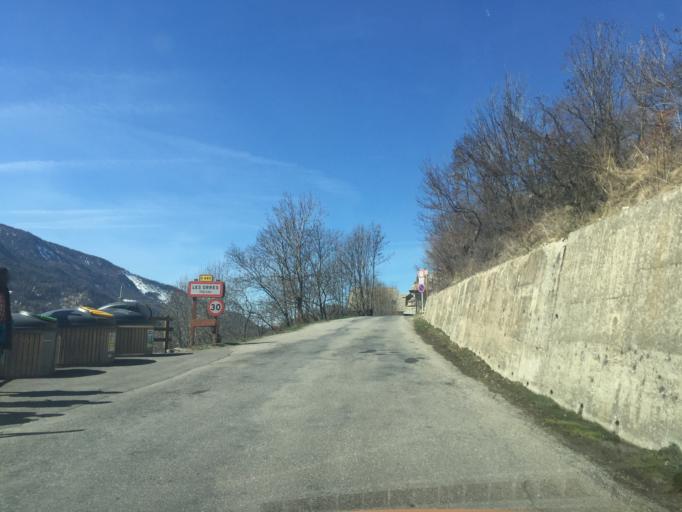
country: FR
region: Provence-Alpes-Cote d'Azur
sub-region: Departement des Hautes-Alpes
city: Embrun
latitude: 44.5129
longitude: 6.5546
